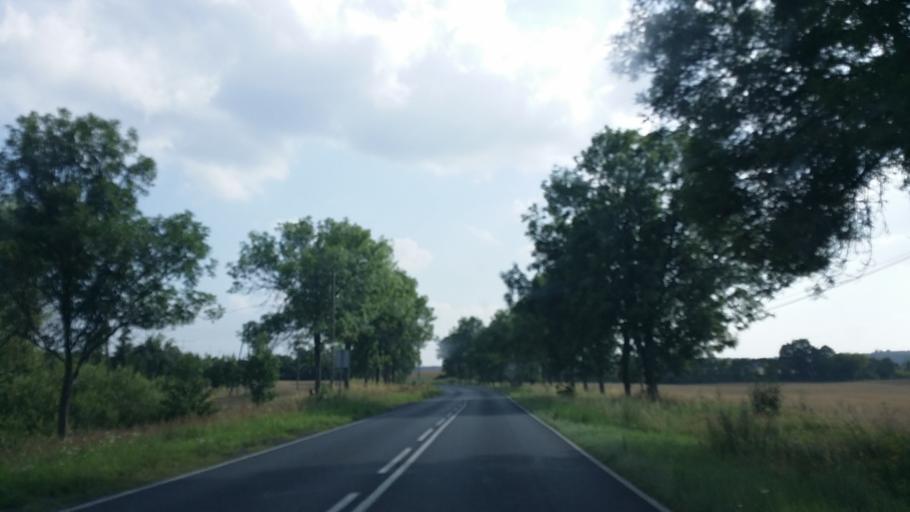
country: PL
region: West Pomeranian Voivodeship
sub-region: Powiat mysliborski
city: Barlinek
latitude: 52.9637
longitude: 15.1836
